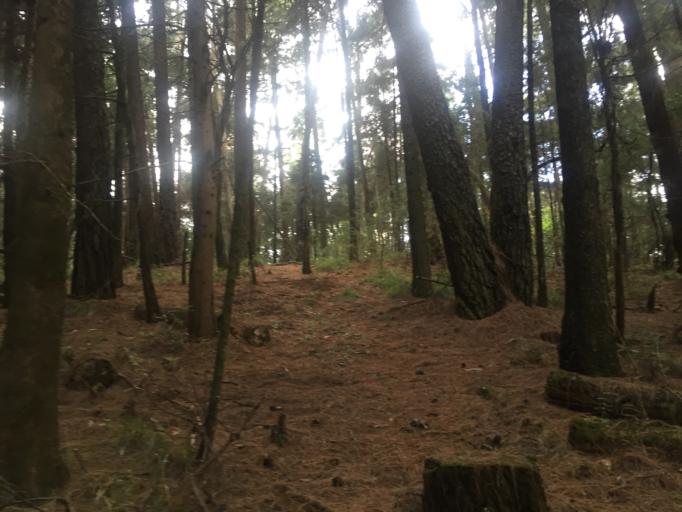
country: MX
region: Mexico City
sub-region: Cuajimalpa de Morelos
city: San Lorenzo Acopilco
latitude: 19.3166
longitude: -99.3080
